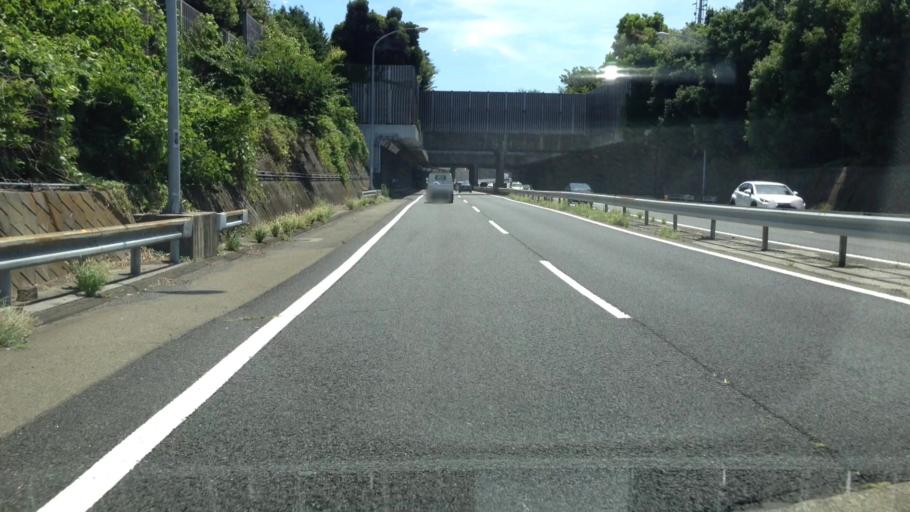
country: JP
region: Kanagawa
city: Yokohama
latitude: 35.4054
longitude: 139.5754
